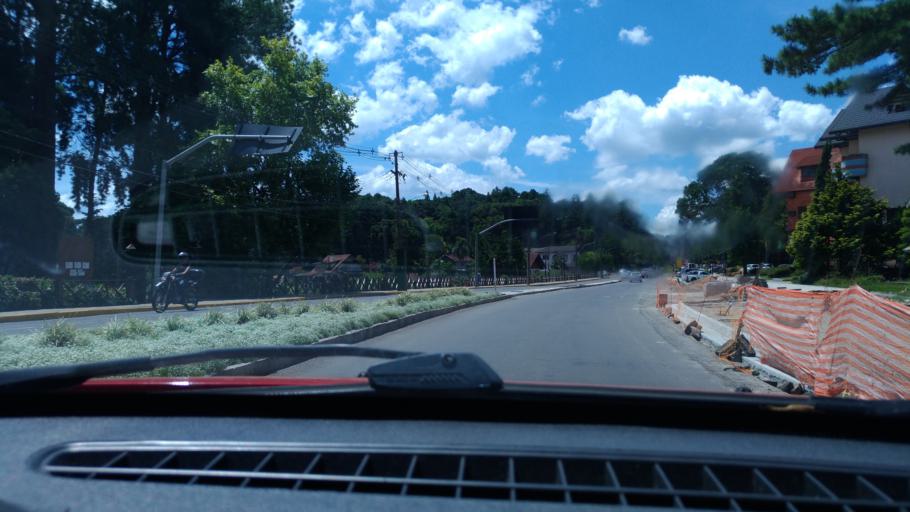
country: BR
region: Rio Grande do Sul
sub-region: Canela
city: Canela
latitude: -29.3878
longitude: -50.8745
